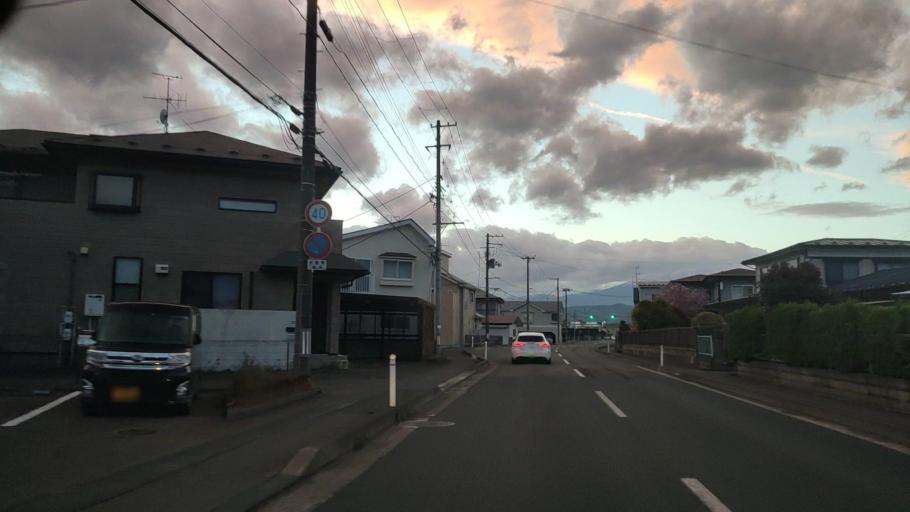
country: JP
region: Iwate
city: Morioka-shi
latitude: 39.7171
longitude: 141.1106
